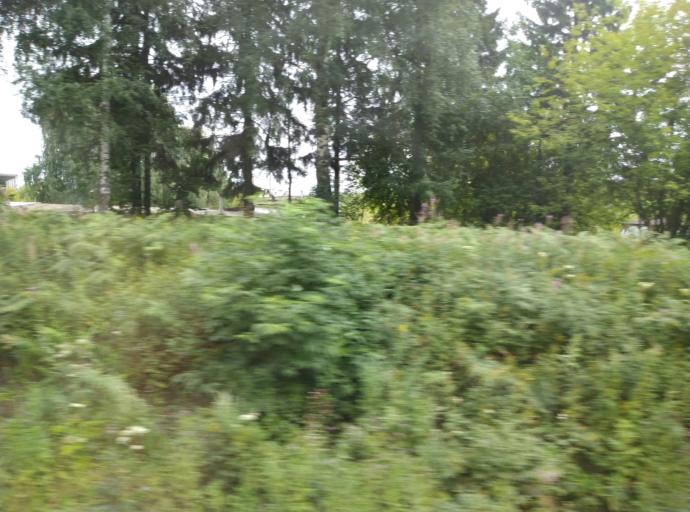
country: RU
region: Kostroma
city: Oktyabr'skiy
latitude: 57.7432
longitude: 40.9700
